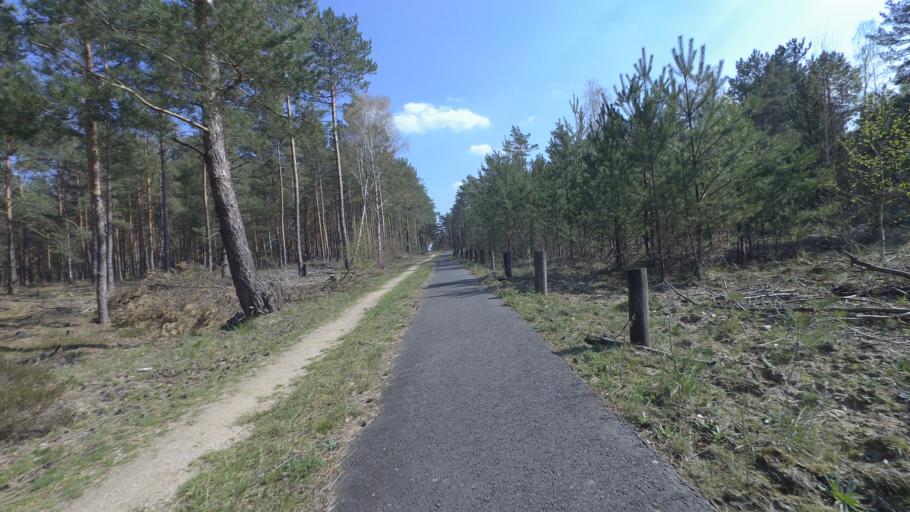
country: DE
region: Brandenburg
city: Mittenwalde
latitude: 52.1888
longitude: 13.5332
